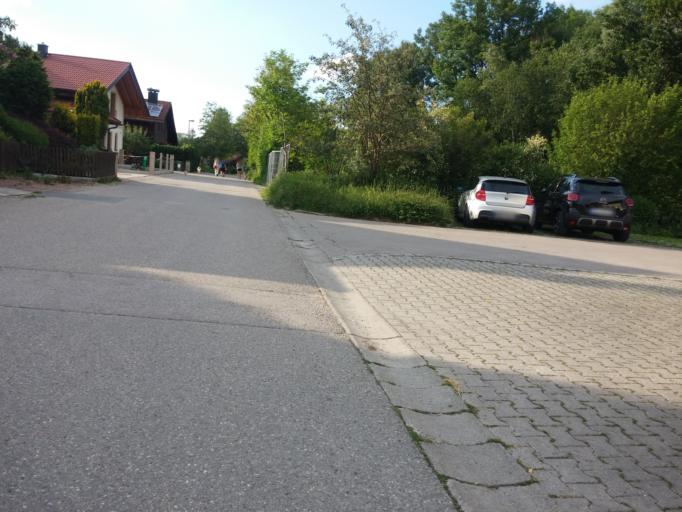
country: DE
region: Bavaria
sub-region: Upper Bavaria
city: Grafing bei Munchen
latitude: 48.0399
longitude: 11.9726
